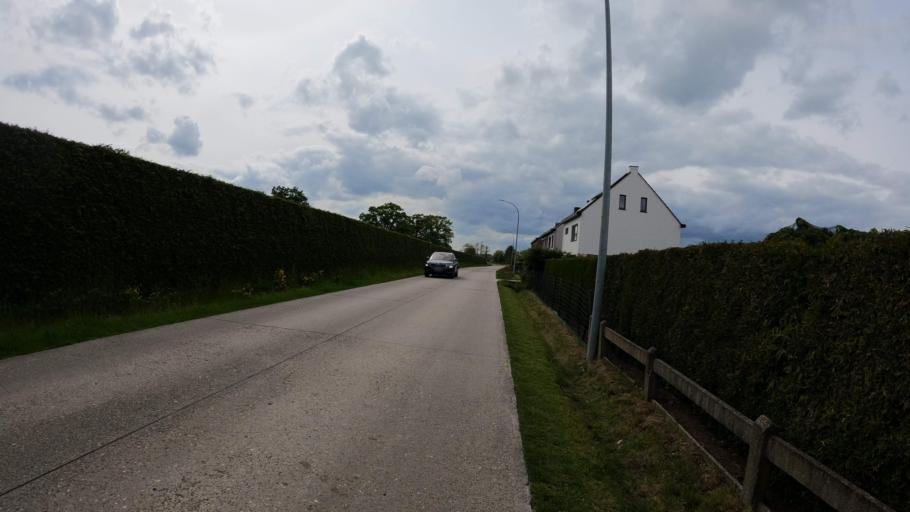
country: BE
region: Flanders
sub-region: Provincie Antwerpen
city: Oud-Turnhout
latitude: 51.3090
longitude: 4.9790
